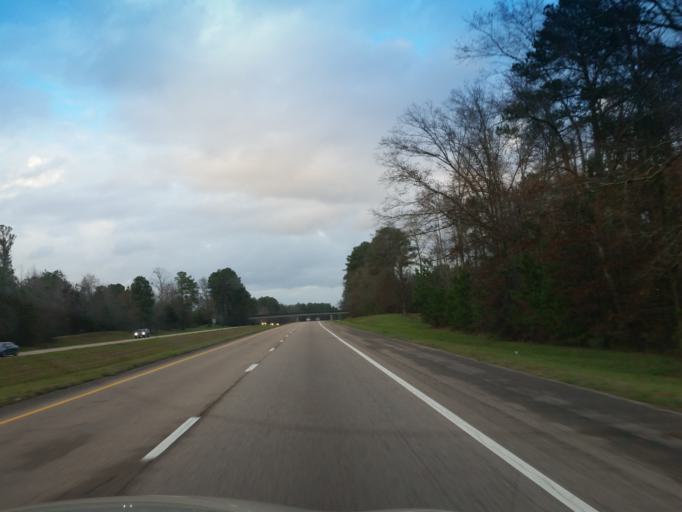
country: US
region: Mississippi
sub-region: Clarke County
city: Stonewall
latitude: 32.0344
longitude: -88.9215
